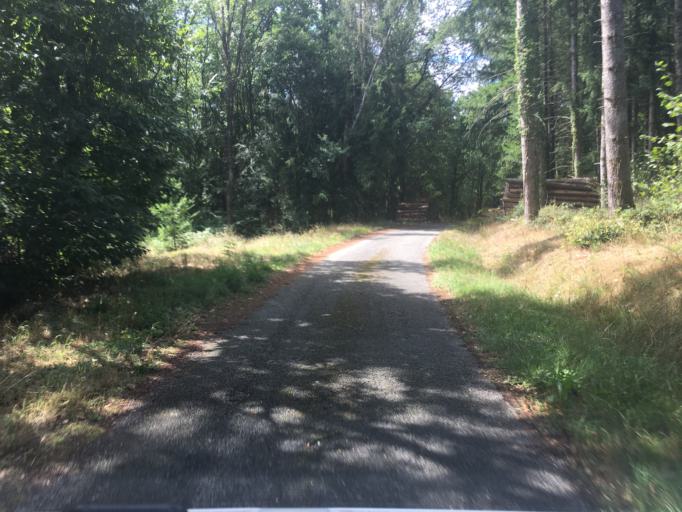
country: FR
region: Auvergne
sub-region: Departement du Cantal
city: Champagnac
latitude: 45.4181
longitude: 2.3812
